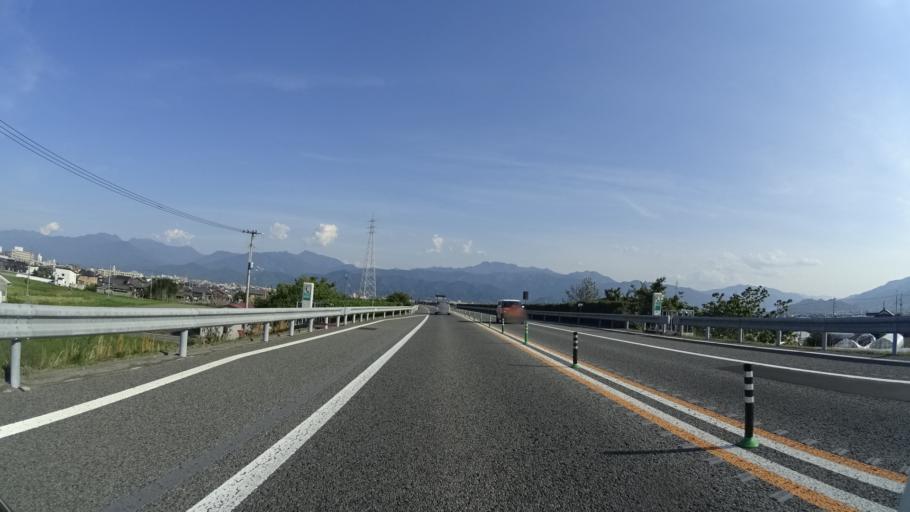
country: JP
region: Ehime
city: Saijo
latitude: 33.9342
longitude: 133.0699
